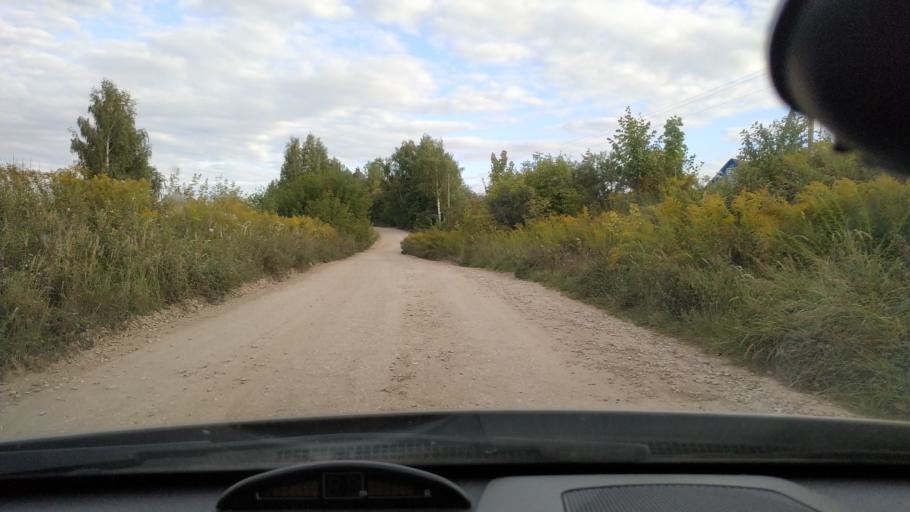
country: RU
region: Rjazan
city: Polyany
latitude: 54.5612
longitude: 39.8757
